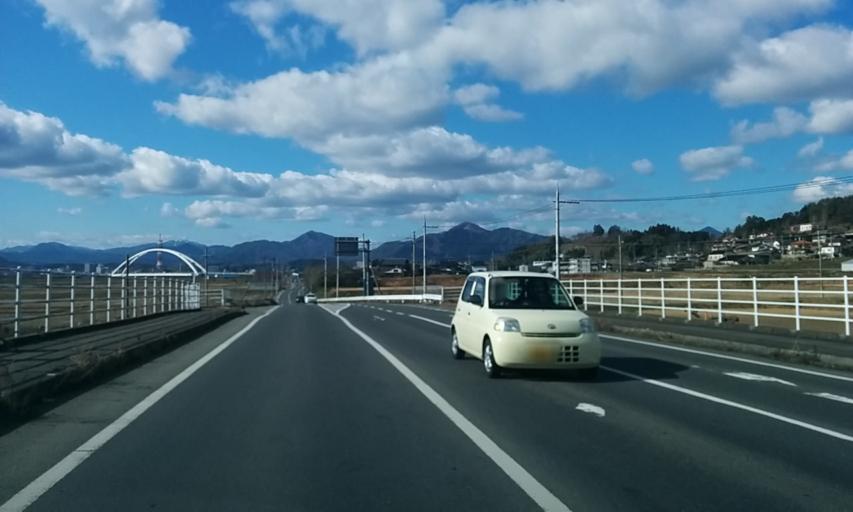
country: JP
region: Kyoto
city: Fukuchiyama
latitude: 35.3050
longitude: 135.1422
